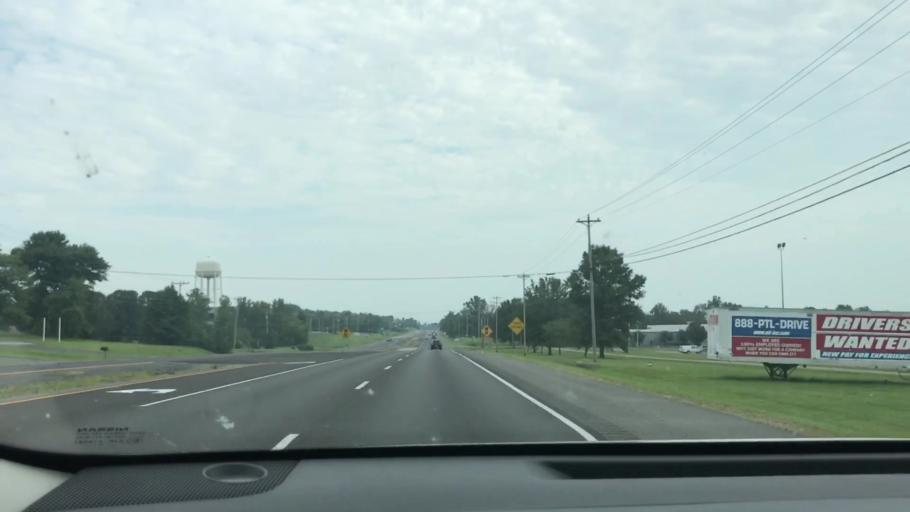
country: US
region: Kentucky
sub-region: Calloway County
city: Murray
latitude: 36.6561
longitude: -88.3062
